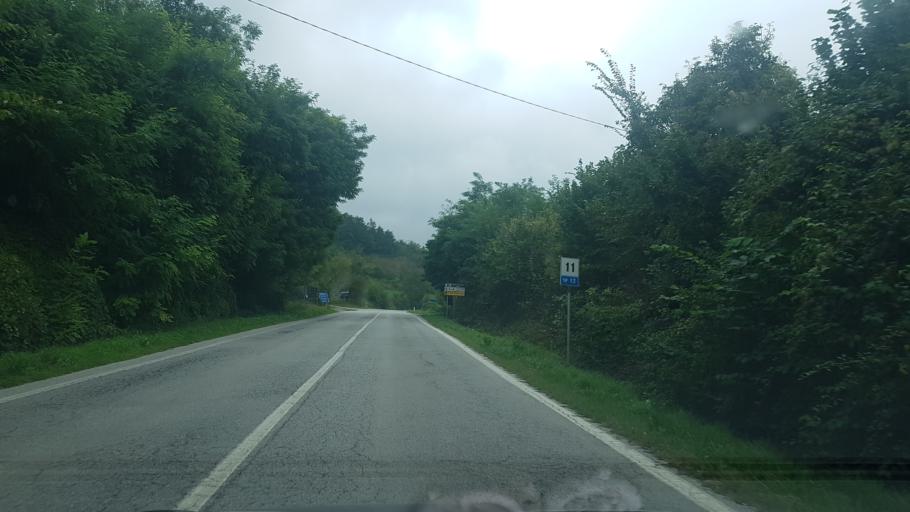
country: IT
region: Piedmont
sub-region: Provincia di Cuneo
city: Bastia Mondovi
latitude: 44.4394
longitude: 7.9025
